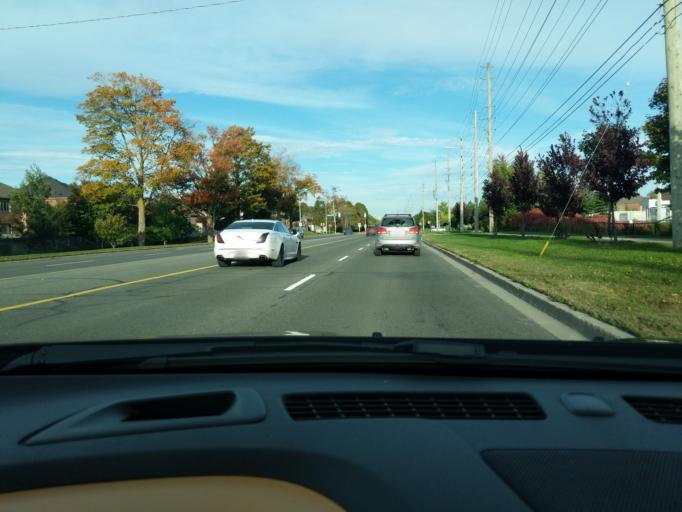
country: CA
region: Ontario
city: Newmarket
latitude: 44.0343
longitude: -79.4848
